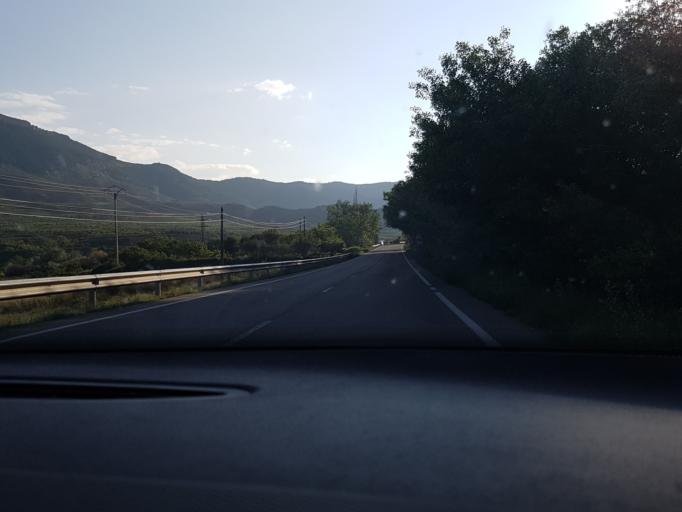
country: ES
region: La Rioja
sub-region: Provincia de La Rioja
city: Santa Eulalia Bajera
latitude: 42.2095
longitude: -2.1842
